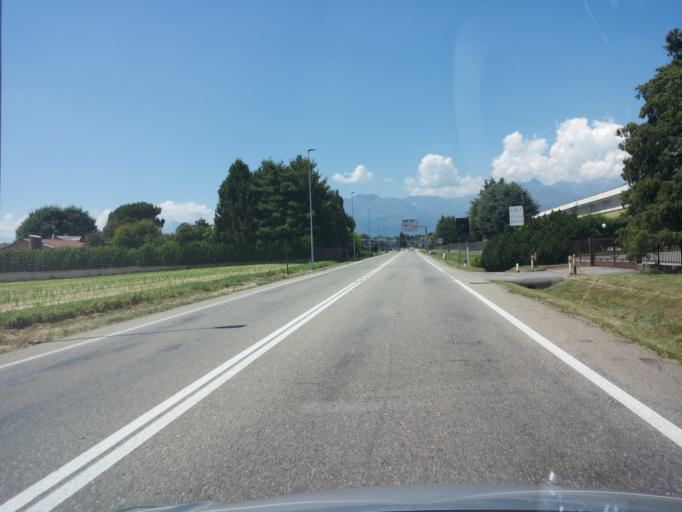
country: IT
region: Piedmont
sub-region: Provincia di Biella
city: Verrone
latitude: 45.5050
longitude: 8.1234
